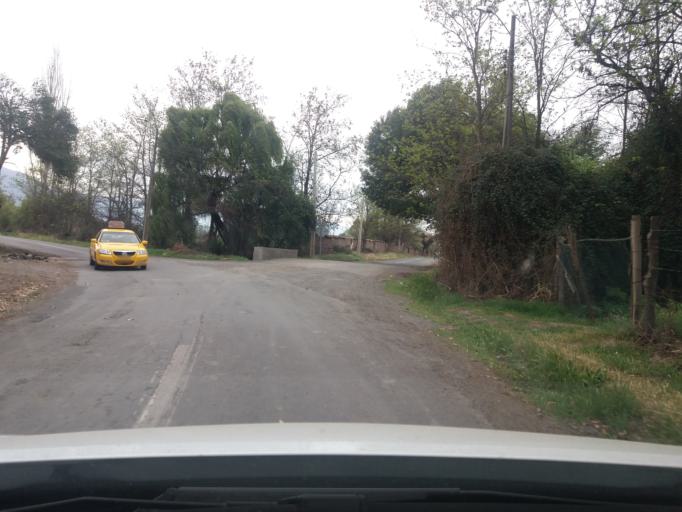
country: CL
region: Valparaiso
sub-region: Provincia de Los Andes
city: Los Andes
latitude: -32.8560
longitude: -70.6505
